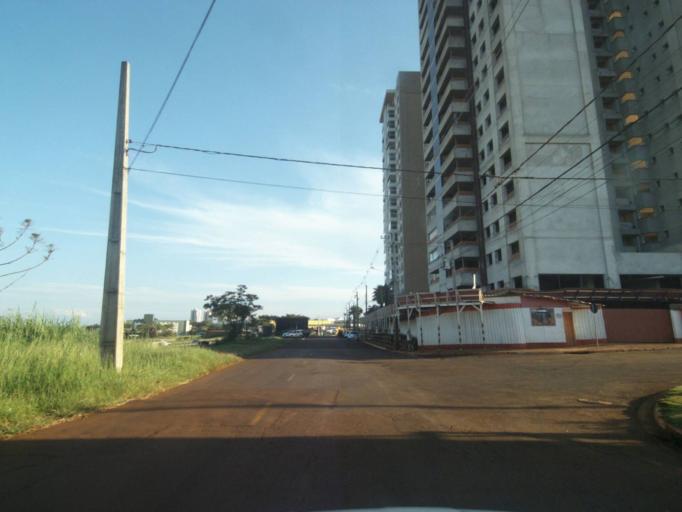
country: BR
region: Parana
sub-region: Londrina
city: Londrina
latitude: -23.3368
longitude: -51.1859
